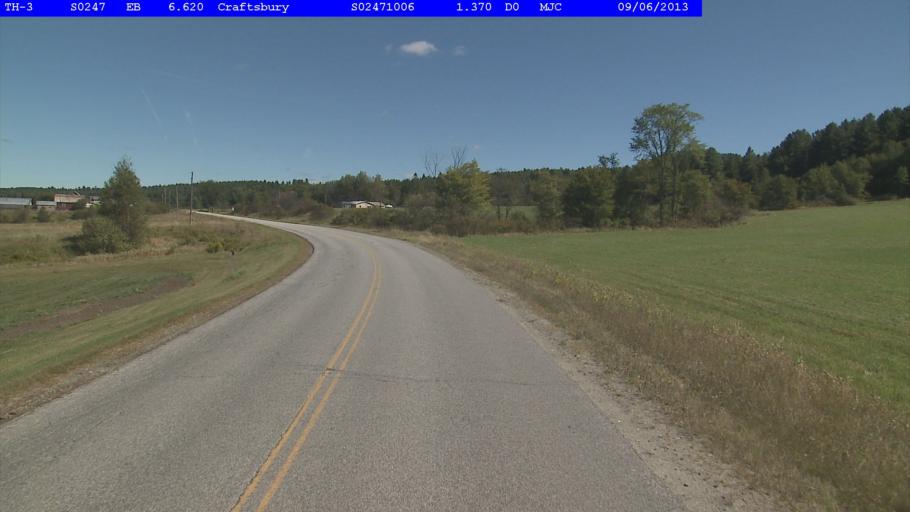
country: US
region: Vermont
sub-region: Caledonia County
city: Hardwick
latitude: 44.6319
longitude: -72.4236
